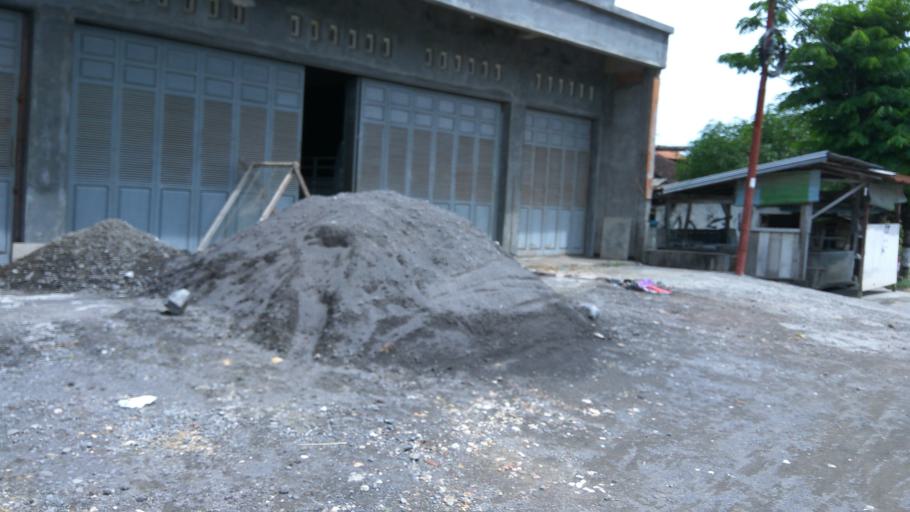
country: ID
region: Central Java
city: Mranggen
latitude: -7.0645
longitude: 110.6659
